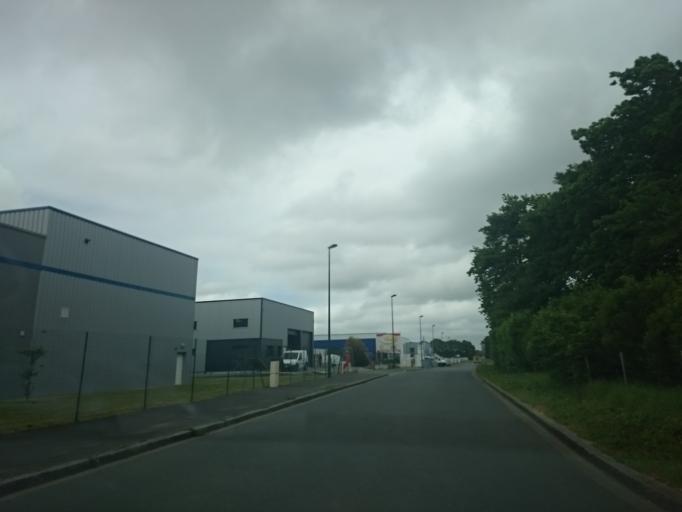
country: FR
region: Pays de la Loire
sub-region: Departement de la Loire-Atlantique
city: Bouaye
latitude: 47.1623
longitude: -1.6795
